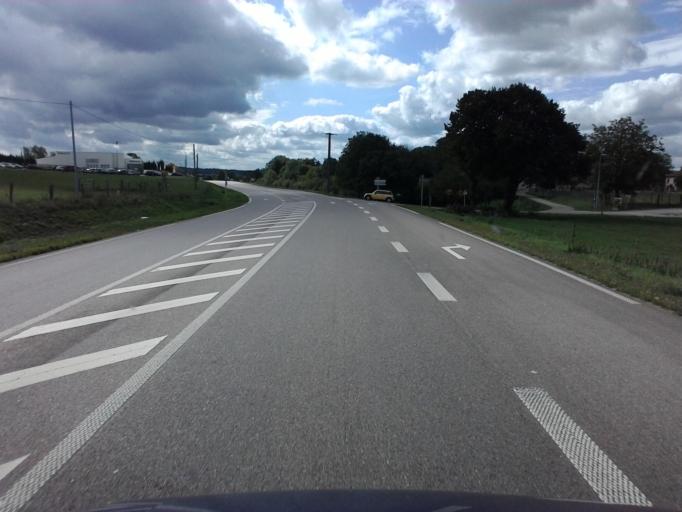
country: FR
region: Lorraine
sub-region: Departement des Vosges
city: Neufchateau
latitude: 48.4102
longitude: 5.7446
